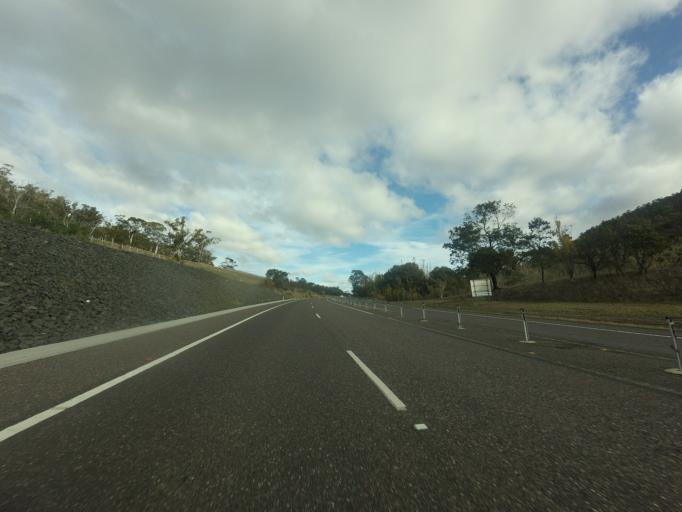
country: AU
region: Tasmania
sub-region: Brighton
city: Bridgewater
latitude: -42.5530
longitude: 147.2102
